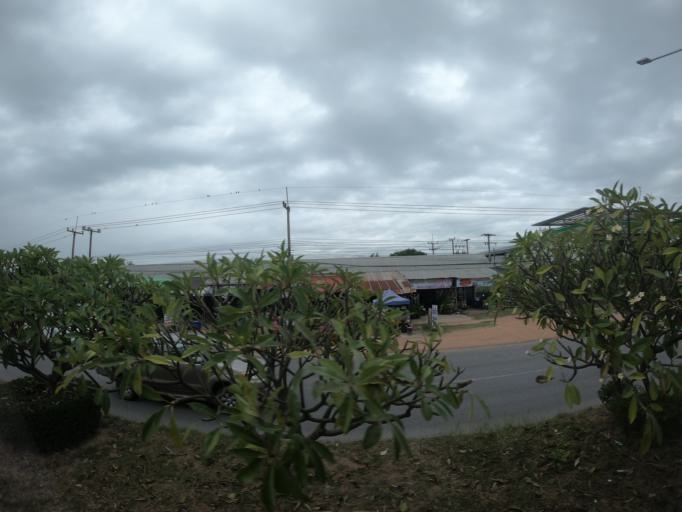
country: TH
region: Maha Sarakham
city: Maha Sarakham
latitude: 16.1722
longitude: 103.2935
